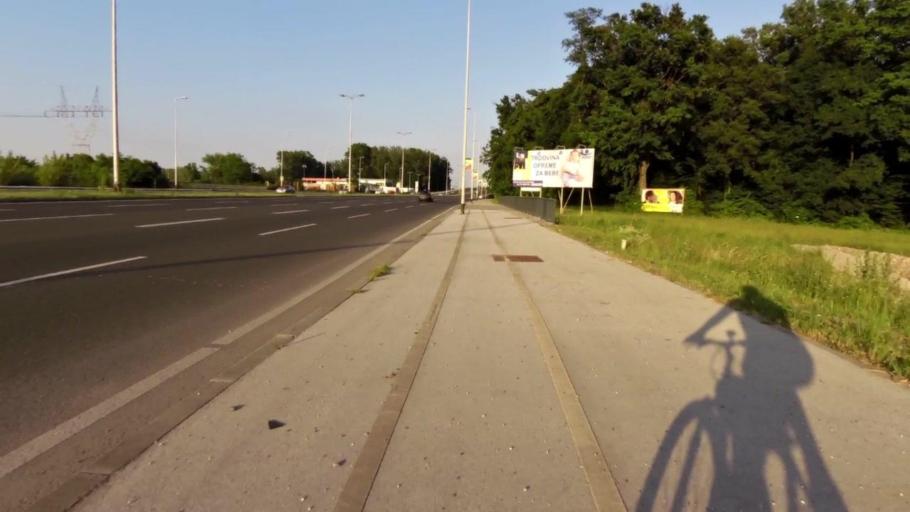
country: HR
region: Grad Zagreb
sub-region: Sesvete
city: Sesvete
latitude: 45.8058
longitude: 16.0936
